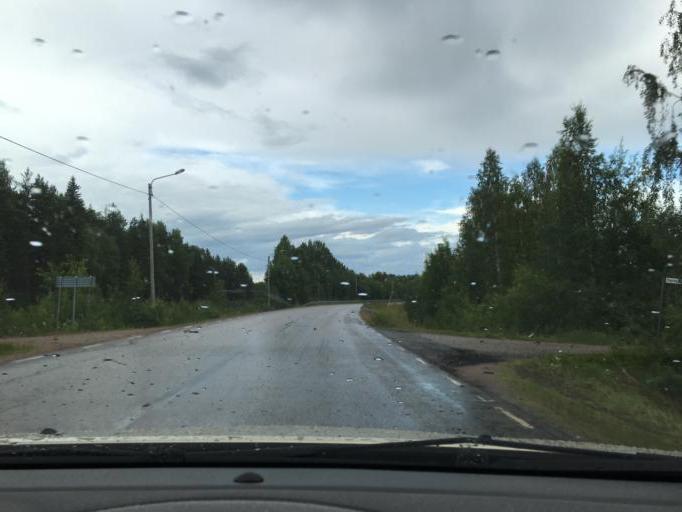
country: SE
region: Norrbotten
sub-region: Kalix Kommun
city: Toere
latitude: 66.0738
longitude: 22.7273
